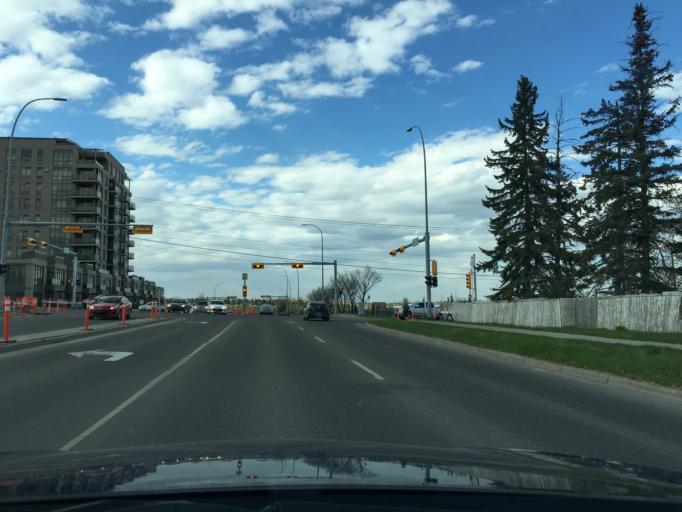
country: CA
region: Alberta
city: Calgary
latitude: 50.9208
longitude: -114.0750
